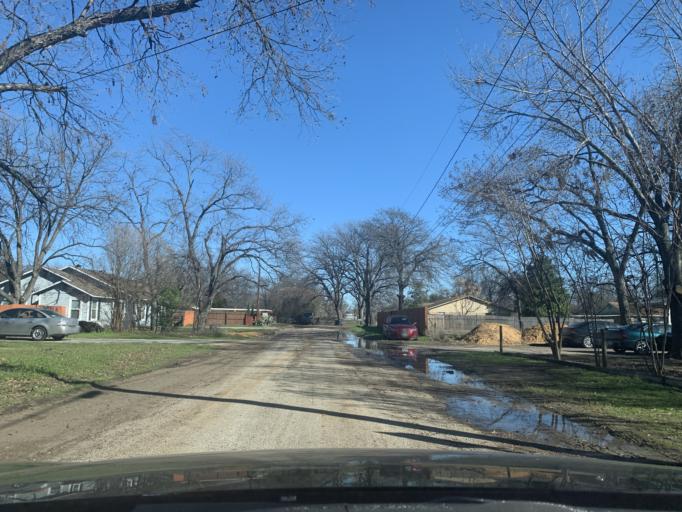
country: US
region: Texas
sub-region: Tarrant County
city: Haltom City
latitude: 32.7833
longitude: -97.2788
